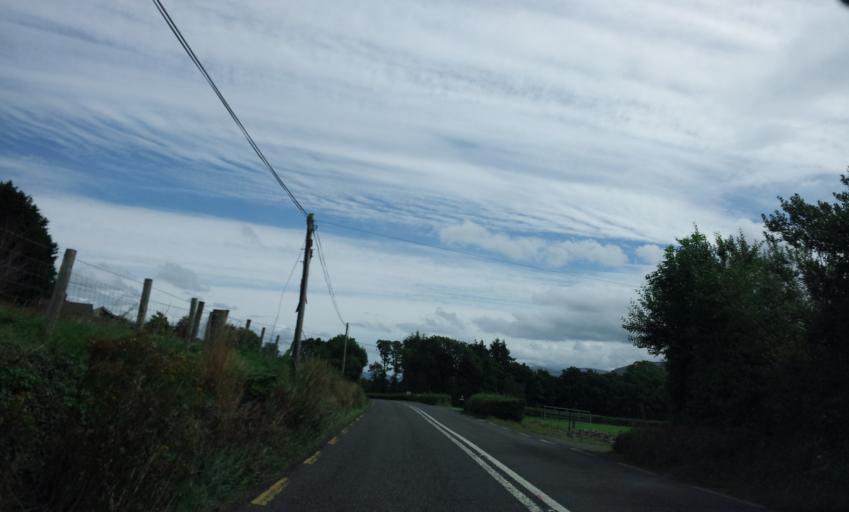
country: IE
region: Munster
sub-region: Ciarrai
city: Killorglin
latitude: 52.0770
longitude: -9.6564
